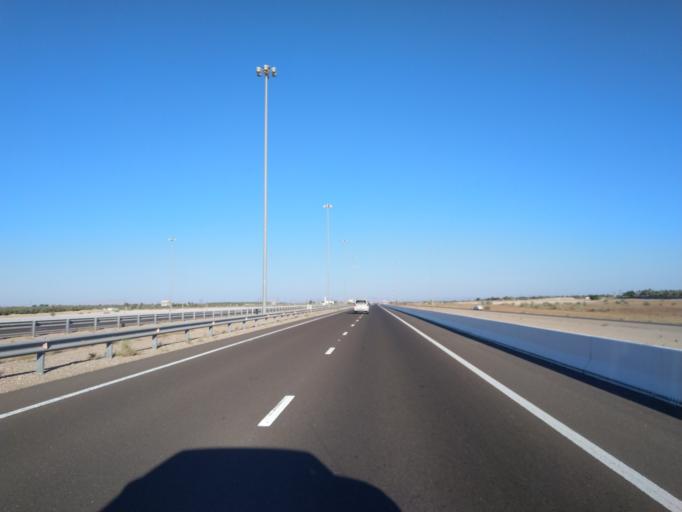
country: OM
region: Al Buraimi
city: Al Buraymi
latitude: 24.5381
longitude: 55.6045
